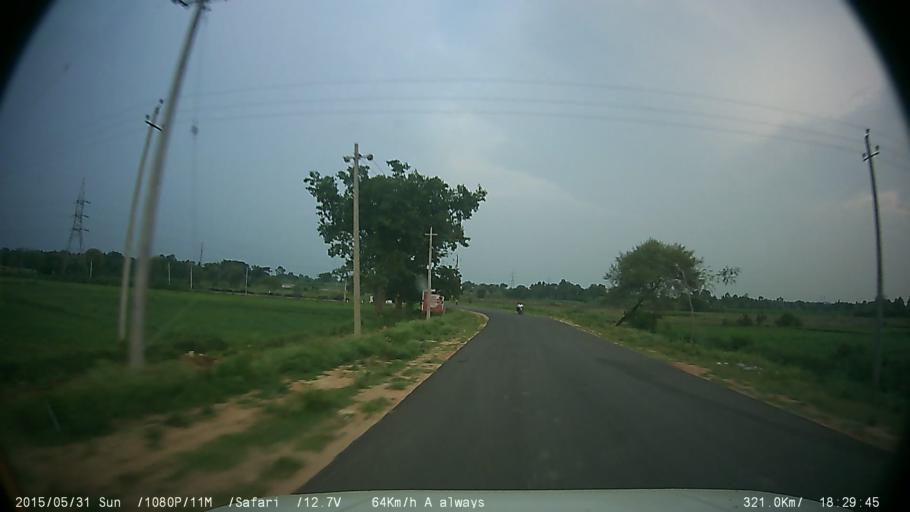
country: IN
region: Karnataka
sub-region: Mysore
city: Nanjangud
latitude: 12.1229
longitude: 76.7333
